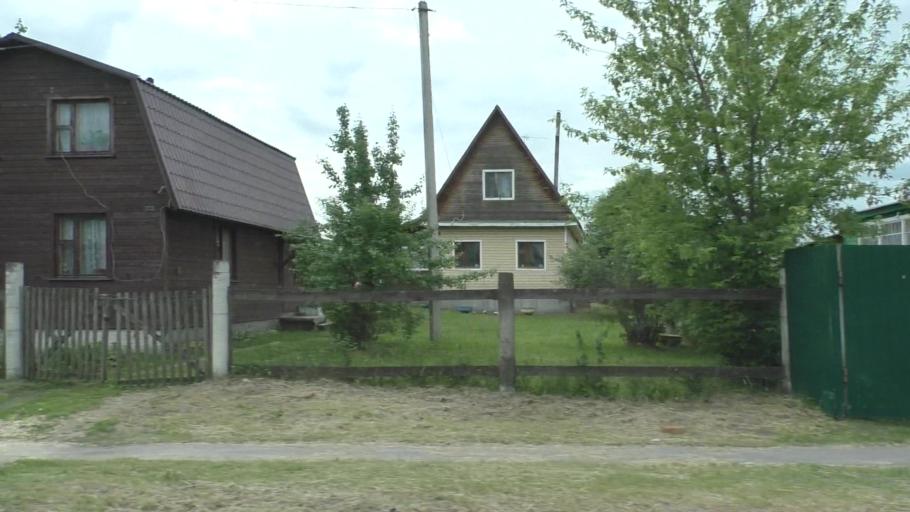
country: RU
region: Moskovskaya
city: Imeni Tsyurupy
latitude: 55.5050
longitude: 38.7768
